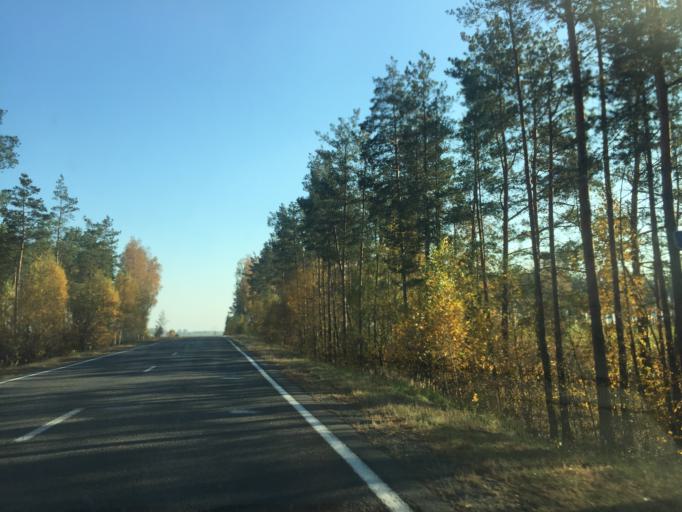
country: BY
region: Gomel
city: Dobrush
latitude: 52.3306
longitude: 31.2394
